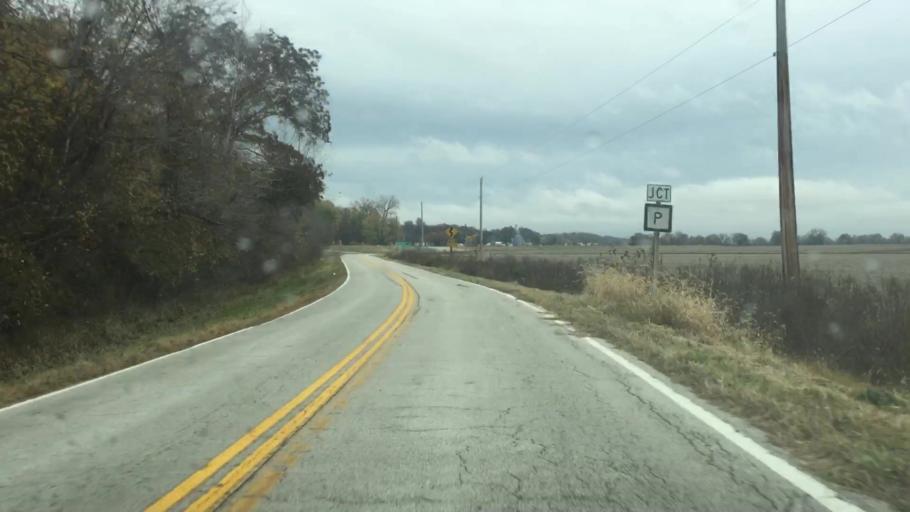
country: US
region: Missouri
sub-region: Gasconade County
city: Hermann
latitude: 38.7120
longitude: -91.5345
